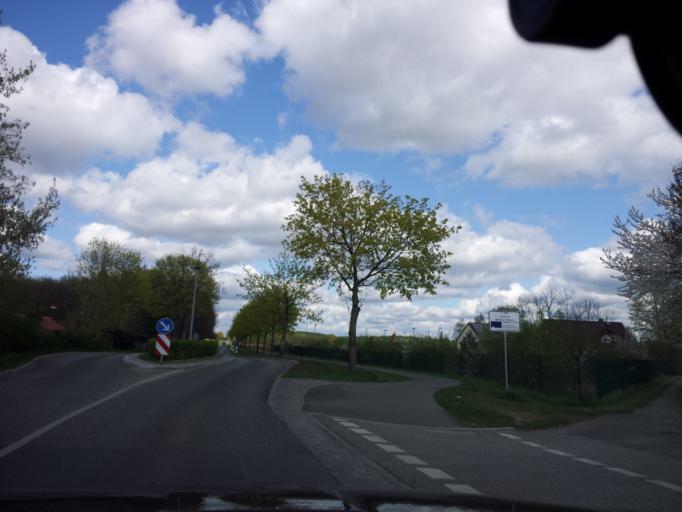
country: DE
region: Brandenburg
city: Bernau bei Berlin
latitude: 52.6890
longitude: 13.6008
